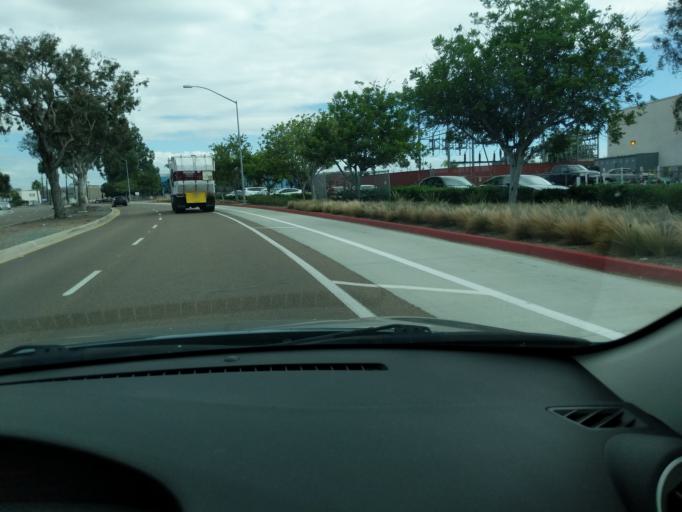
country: US
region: California
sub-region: San Diego County
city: San Diego
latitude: 32.8203
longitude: -117.1410
